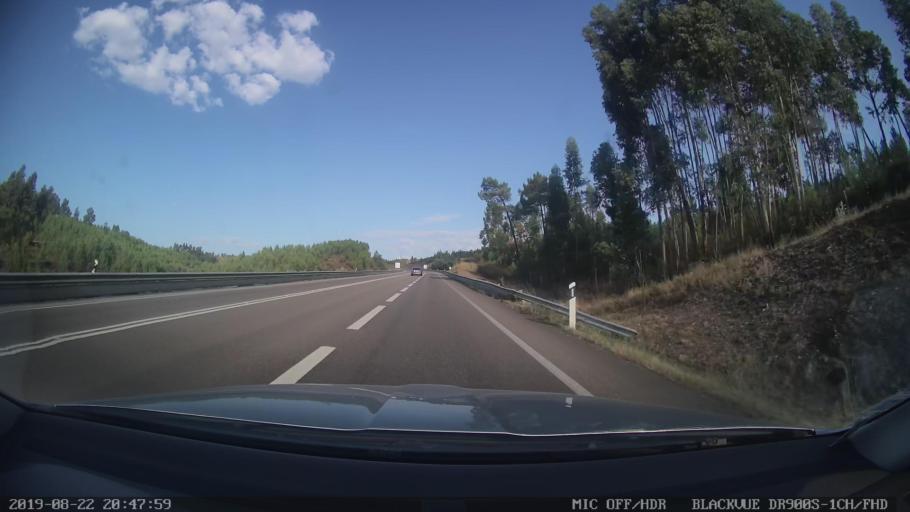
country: PT
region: Castelo Branco
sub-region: Proenca-A-Nova
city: Proenca-a-Nova
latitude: 39.7347
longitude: -7.8990
